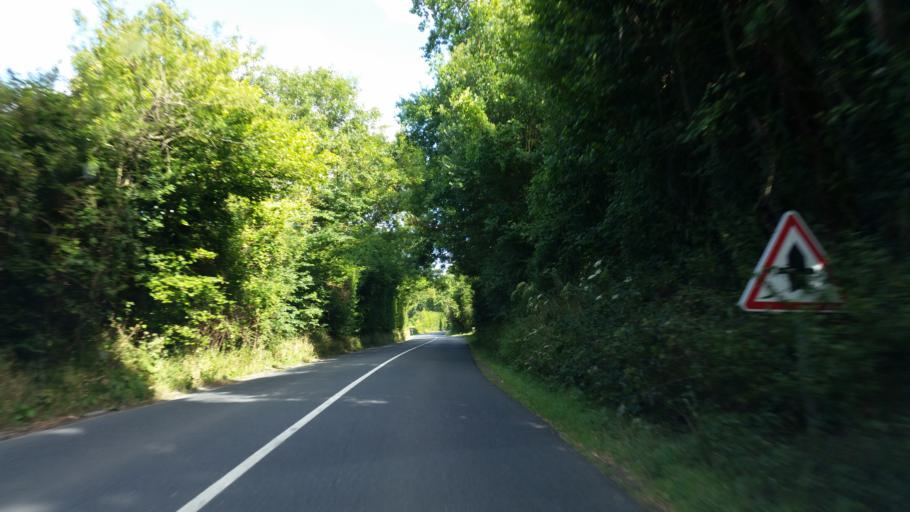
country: FR
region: Lower Normandy
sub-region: Departement du Calvados
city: Dives-sur-Mer
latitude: 49.2586
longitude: -0.0912
